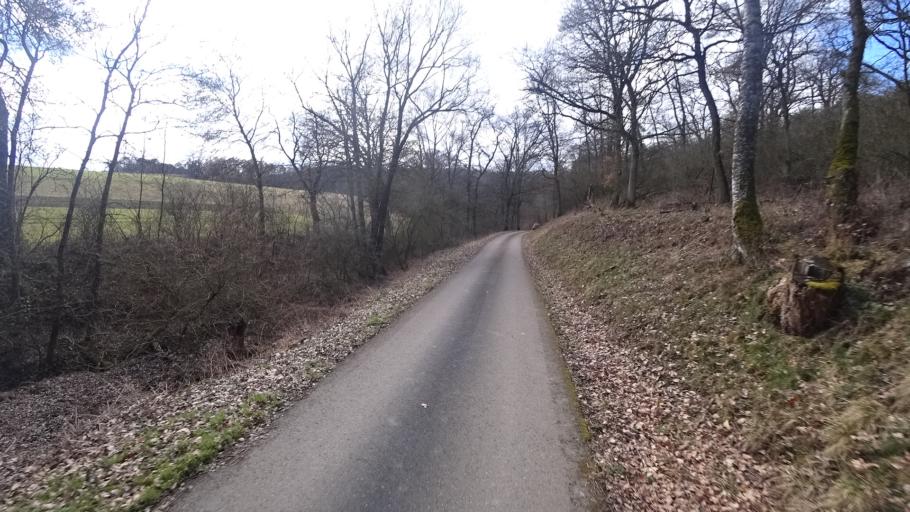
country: DE
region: Rheinland-Pfalz
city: Reichenberg
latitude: 50.1430
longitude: 7.7579
